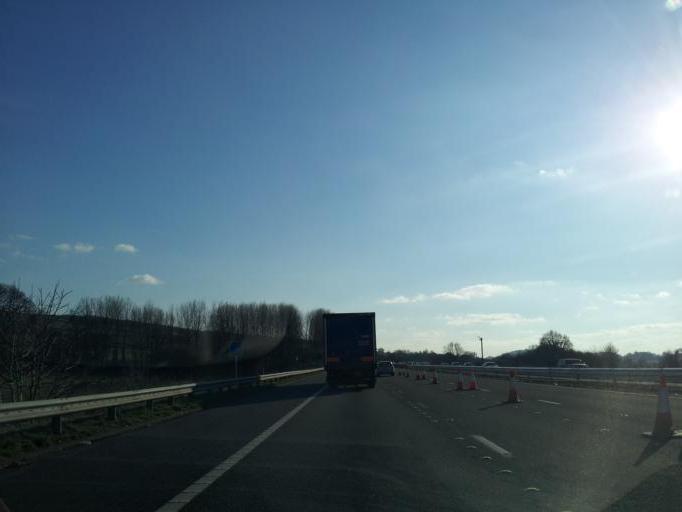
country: GB
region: England
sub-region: Devon
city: Bradninch
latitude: 50.8216
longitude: -3.4070
